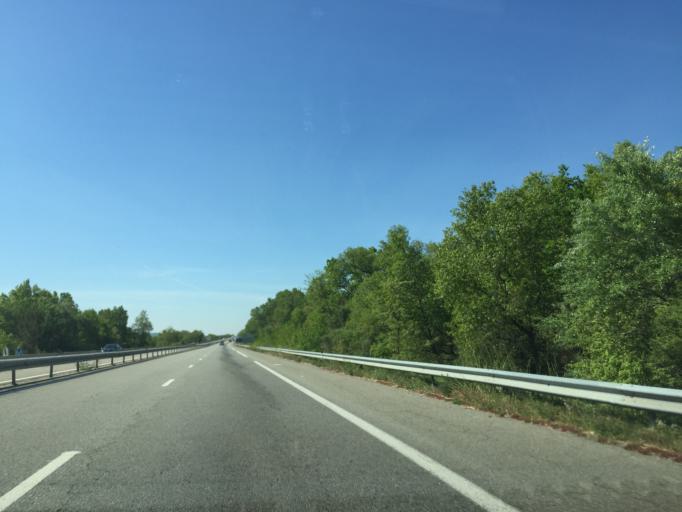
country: FR
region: Provence-Alpes-Cote d'Azur
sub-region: Departement des Alpes-de-Haute-Provence
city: Oraison
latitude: 43.9144
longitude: 5.8888
